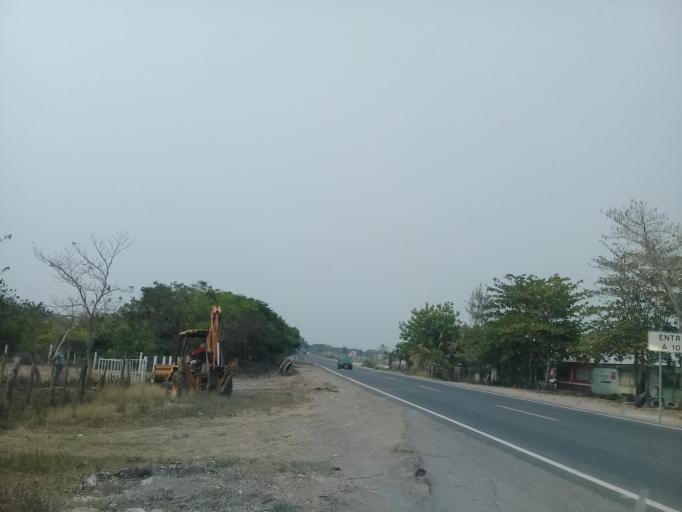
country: MX
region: Veracruz
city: Paso del Toro
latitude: 18.9819
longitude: -96.1742
